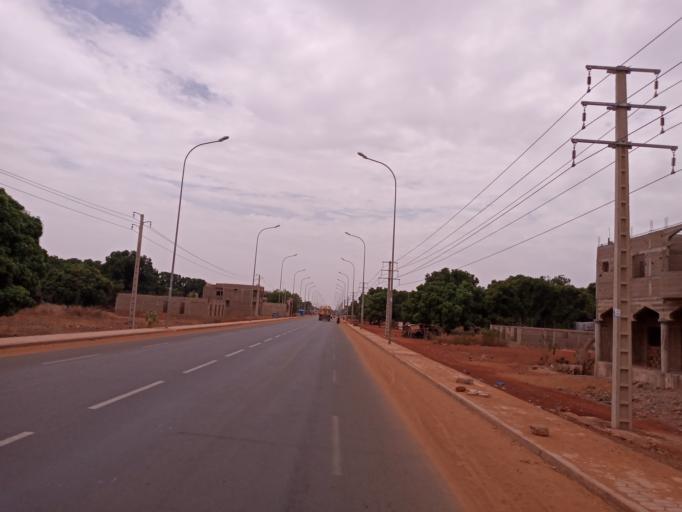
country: ML
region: Koulikoro
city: Koulikoro
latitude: 12.8478
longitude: -7.5769
